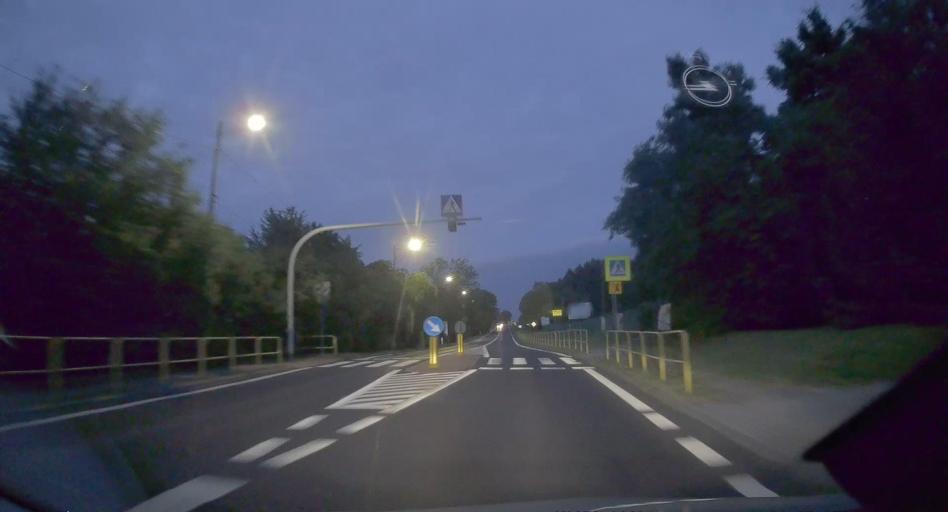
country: PL
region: Silesian Voivodeship
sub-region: Powiat klobucki
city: Kamyk
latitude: 50.8832
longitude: 18.9871
